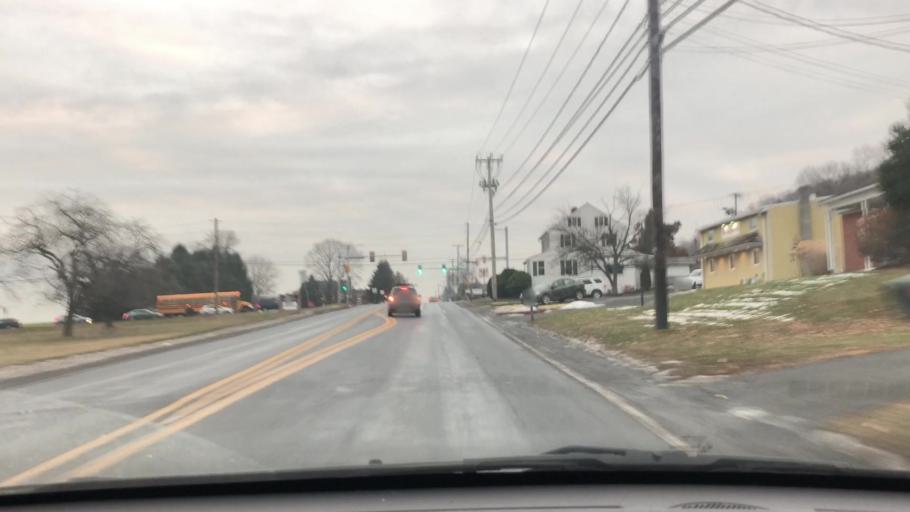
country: US
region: Pennsylvania
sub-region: Lancaster County
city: Mountville
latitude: 40.0652
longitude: -76.4589
